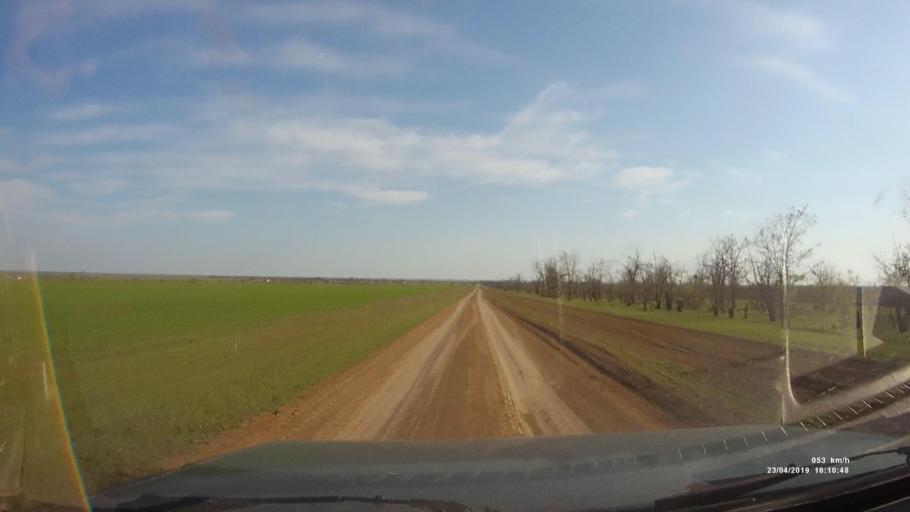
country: RU
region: Rostov
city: Remontnoye
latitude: 46.4794
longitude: 43.1231
